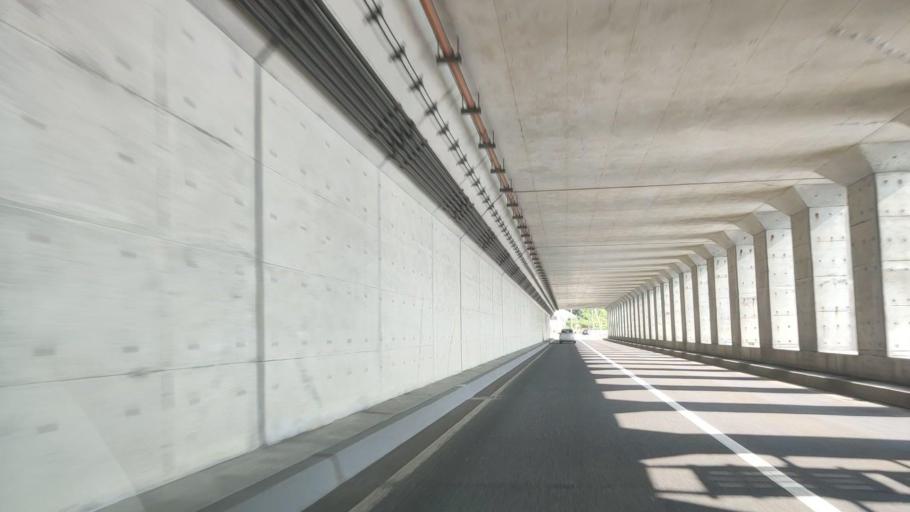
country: JP
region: Hokkaido
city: Rumoi
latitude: 43.6681
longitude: 141.3494
